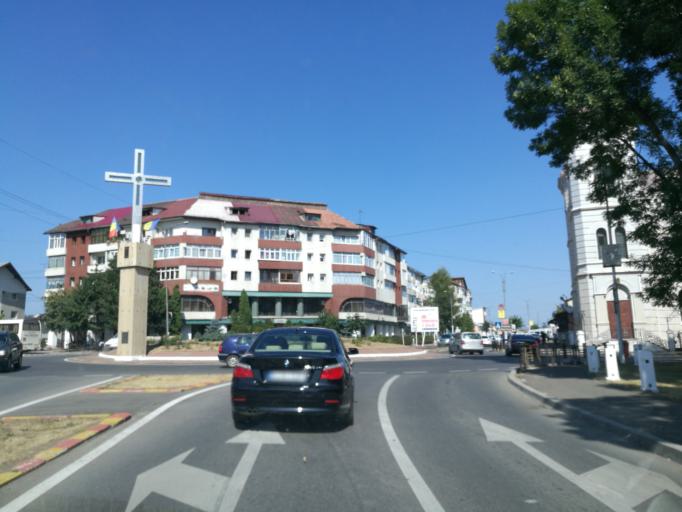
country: RO
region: Suceava
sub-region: Municipiul Suceava
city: Radauti
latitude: 47.8465
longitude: 25.9142
